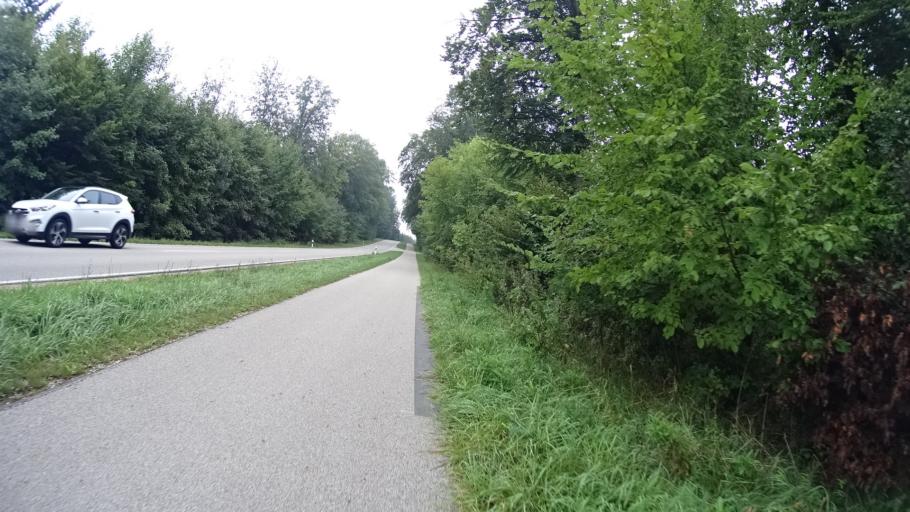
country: DE
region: Bavaria
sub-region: Upper Bavaria
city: Denkendorf
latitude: 48.9019
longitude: 11.4570
